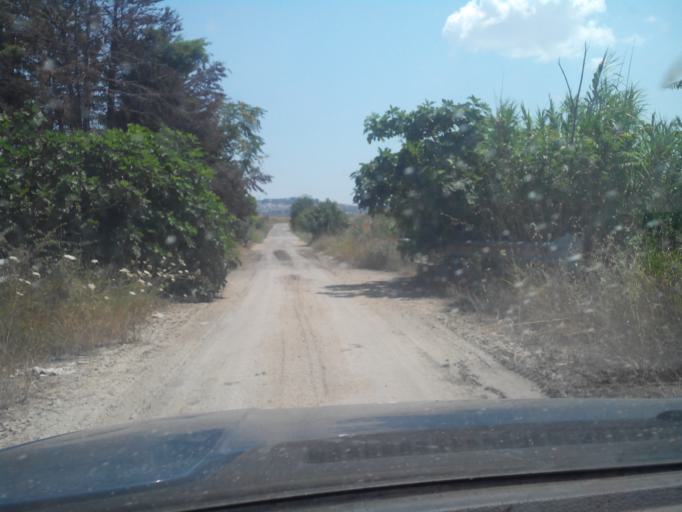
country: IT
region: Basilicate
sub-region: Provincia di Matera
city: La Martella
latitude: 40.6888
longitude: 16.5429
